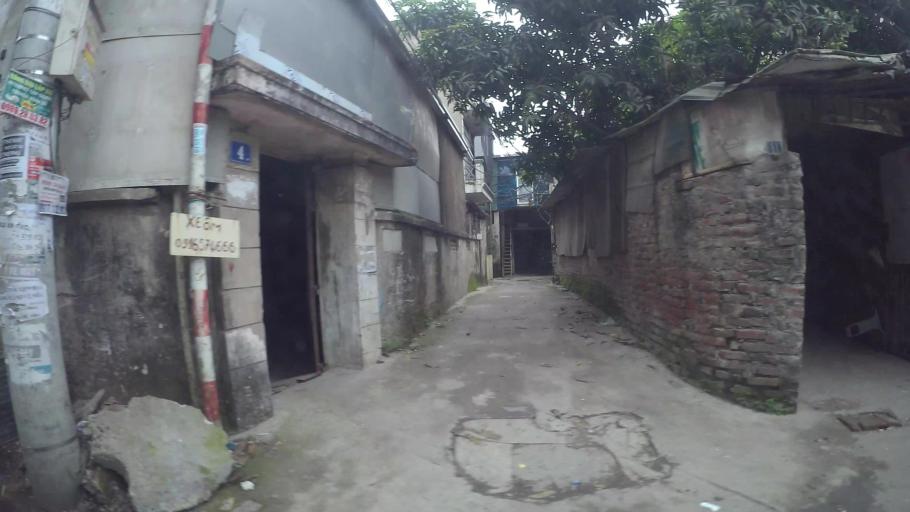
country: VN
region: Ha Noi
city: Hai BaTrung
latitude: 20.9849
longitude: 105.8882
